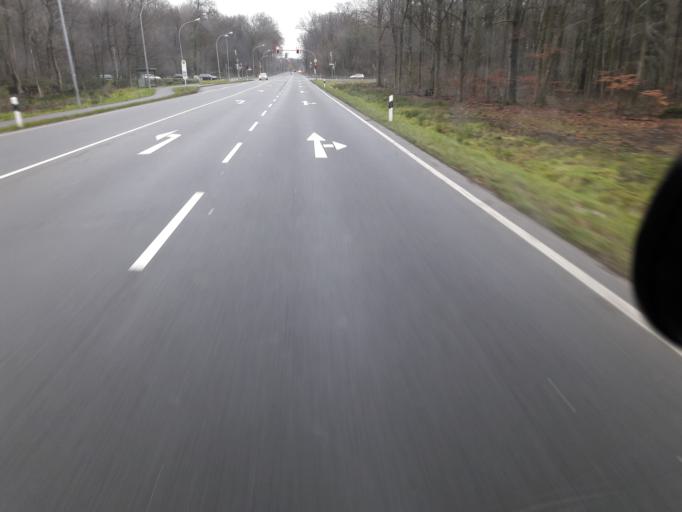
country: DE
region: Lower Saxony
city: Bad Bentheim
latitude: 52.3164
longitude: 7.1580
